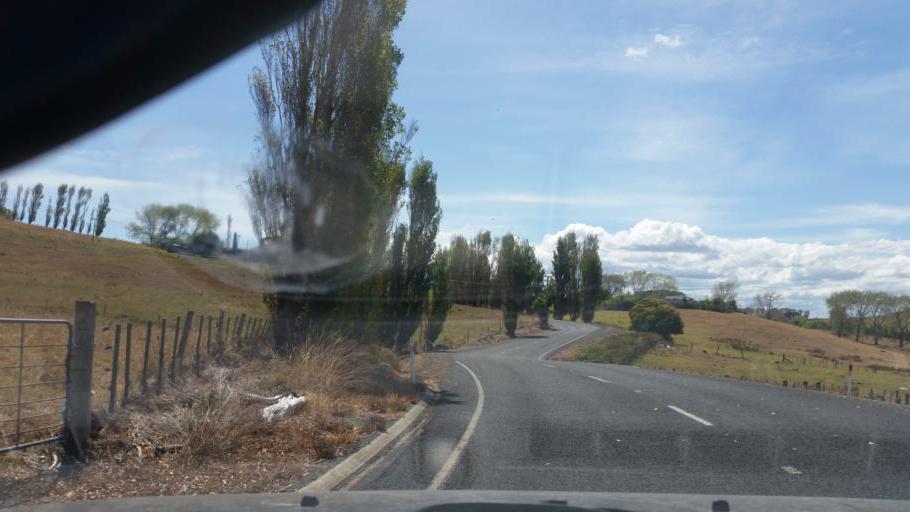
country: NZ
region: Northland
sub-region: Kaipara District
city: Dargaville
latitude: -36.1650
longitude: 174.1664
